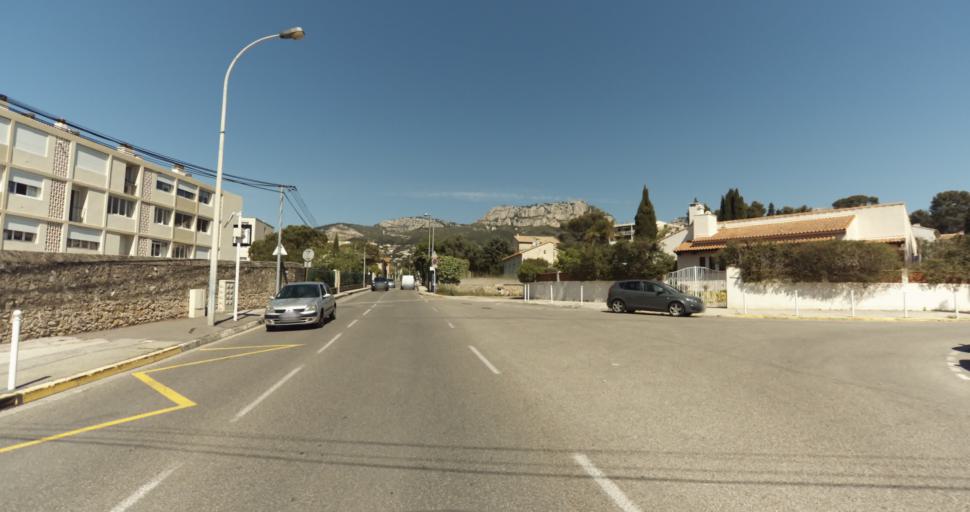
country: FR
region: Provence-Alpes-Cote d'Azur
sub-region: Departement du Var
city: Toulon
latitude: 43.1430
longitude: 5.9082
